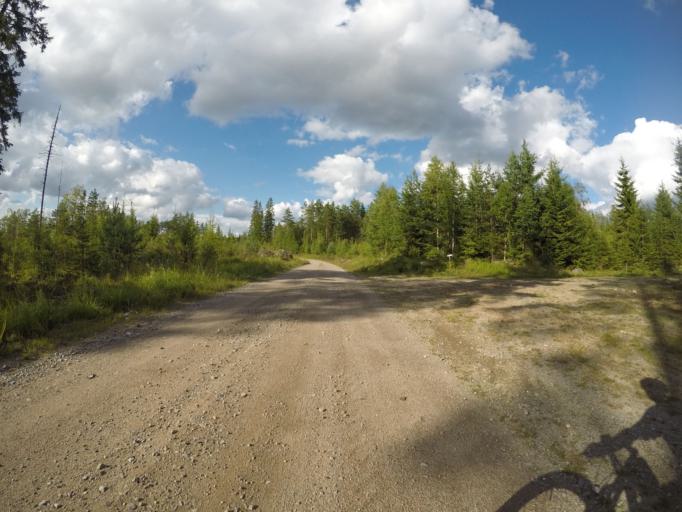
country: SE
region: OErebro
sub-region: Hallefors Kommun
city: Haellefors
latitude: 59.9257
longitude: 14.5678
